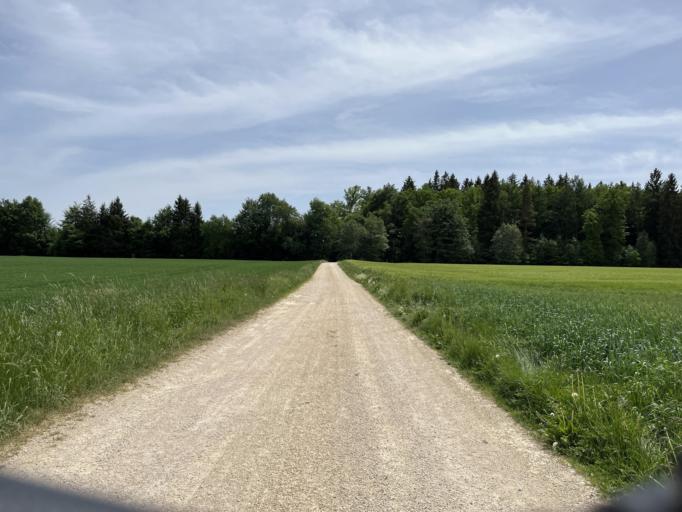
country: DE
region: Baden-Wuerttemberg
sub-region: Tuebingen Region
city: Bingen
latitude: 48.0920
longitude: 9.2658
